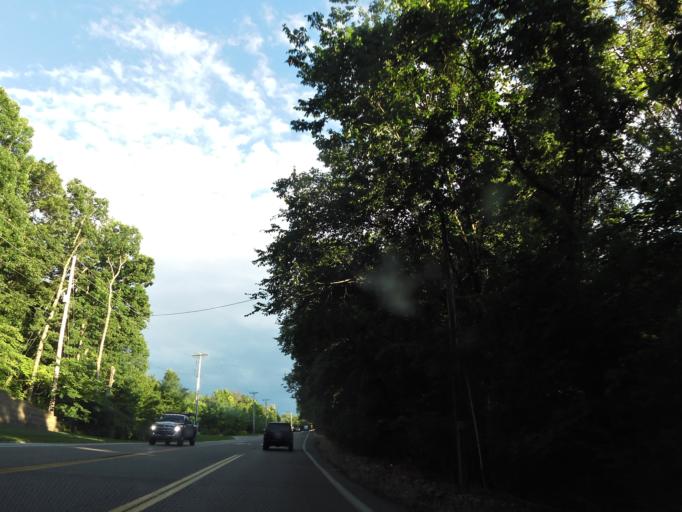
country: US
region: Missouri
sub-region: Saint Louis County
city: Wildwood
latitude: 38.6213
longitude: -90.6559
